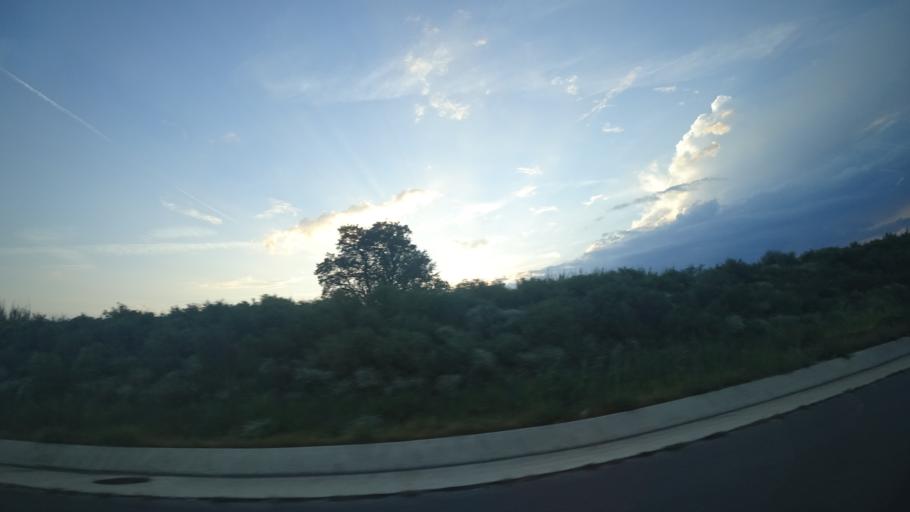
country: FR
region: Languedoc-Roussillon
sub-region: Departement de l'Herault
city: Tourbes
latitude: 43.4325
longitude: 3.3917
